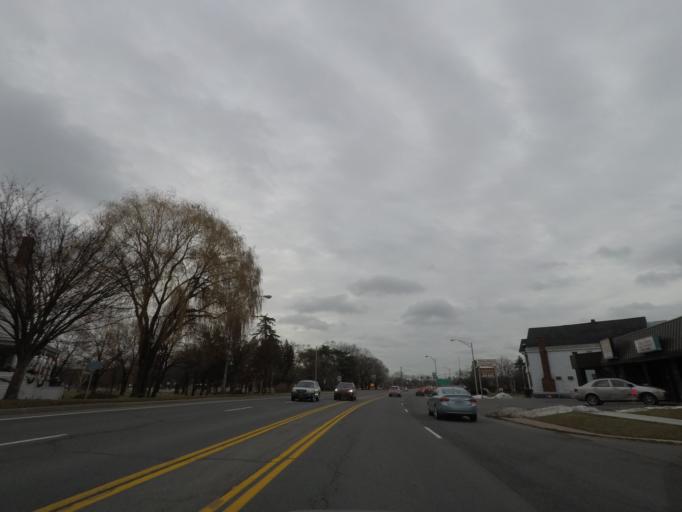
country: US
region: New York
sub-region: Schenectady County
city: Scotia
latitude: 42.8241
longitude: -73.9595
